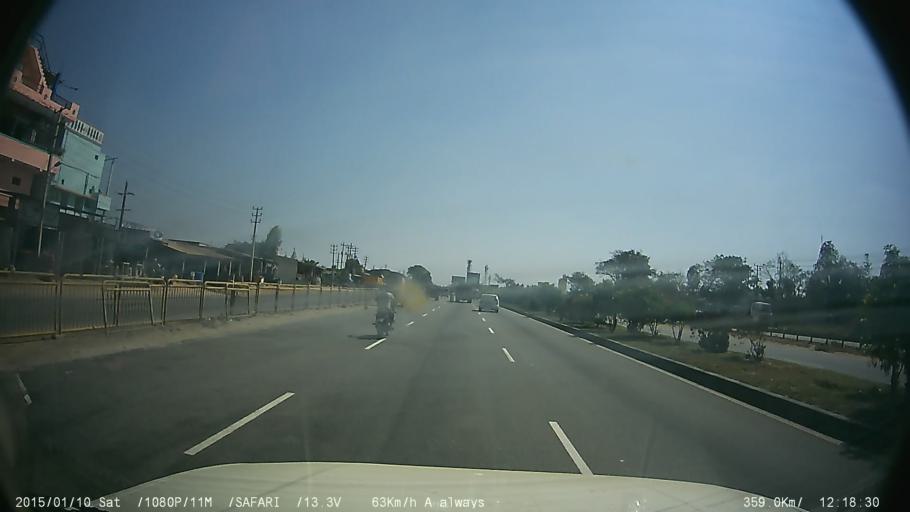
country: IN
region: Karnataka
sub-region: Bangalore Urban
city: Anekal
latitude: 12.7909
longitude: 77.7318
